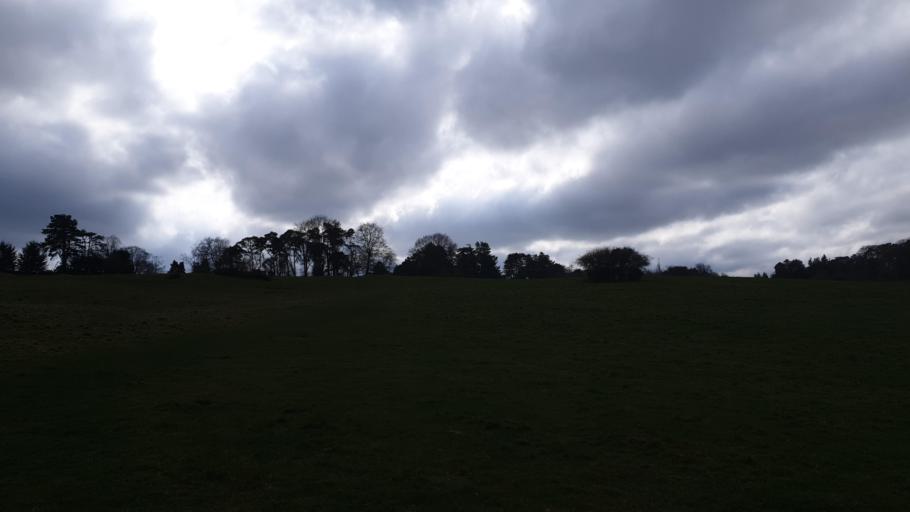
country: GB
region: England
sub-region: Oxfordshire
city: Boars Hill
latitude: 51.7173
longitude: -1.2840
